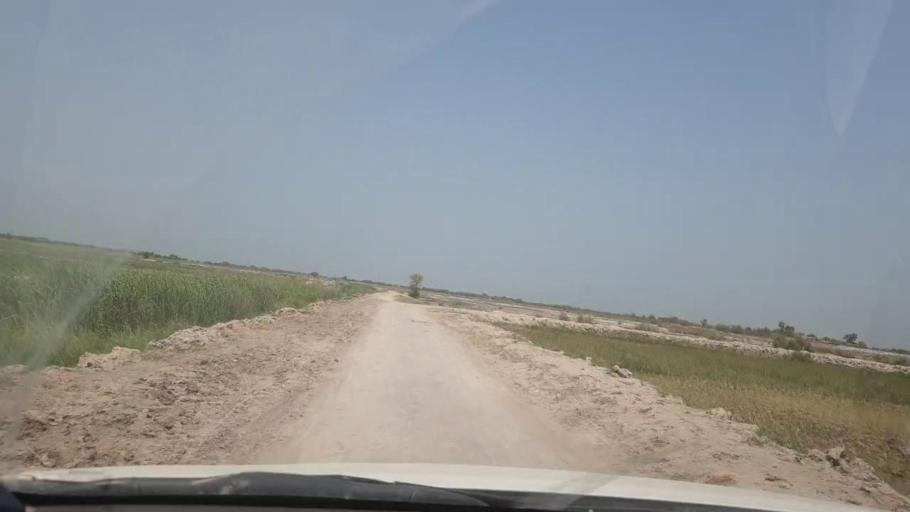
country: PK
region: Sindh
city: Lakhi
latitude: 27.8828
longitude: 68.7374
